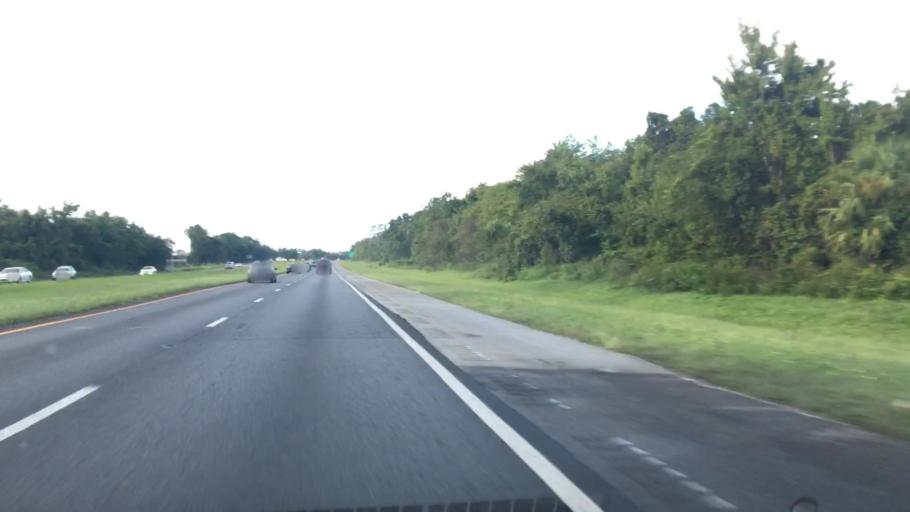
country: US
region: Florida
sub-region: Seminole County
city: Oviedo
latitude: 28.6369
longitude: -81.2432
